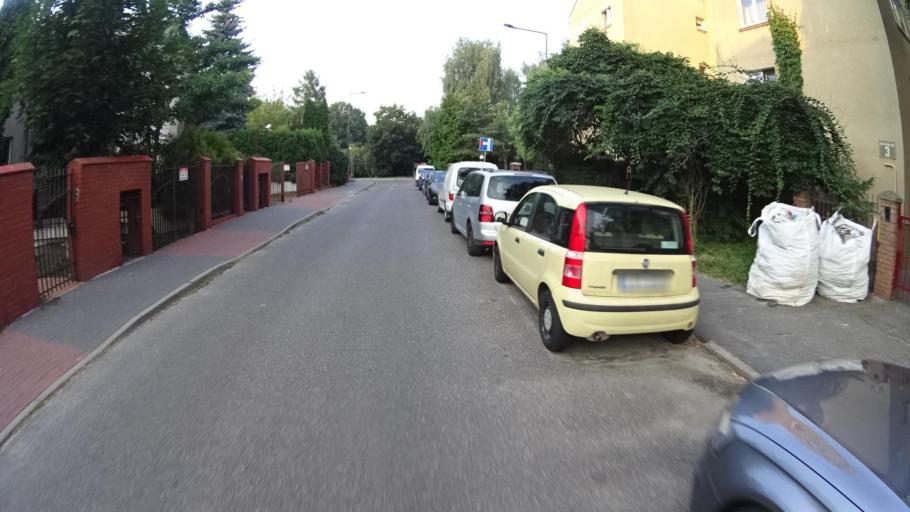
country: PL
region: Masovian Voivodeship
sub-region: Warszawa
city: Ursynow
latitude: 52.1461
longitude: 21.0653
